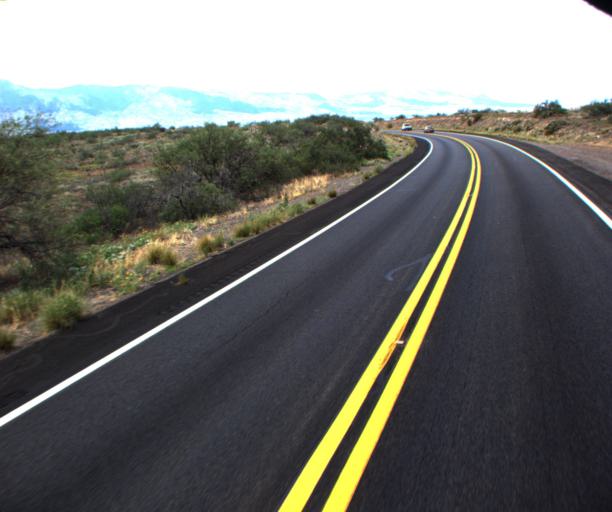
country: US
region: Arizona
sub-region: Yavapai County
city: Camp Verde
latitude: 34.5123
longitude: -111.7443
